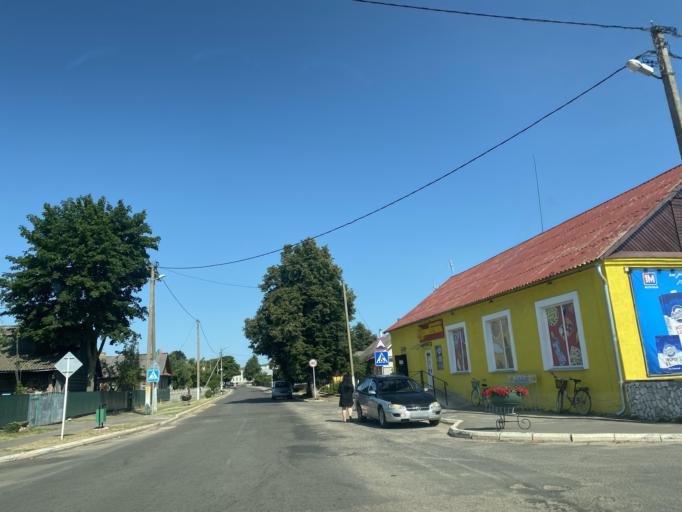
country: BY
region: Brest
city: Ivanava
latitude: 52.3151
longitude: 25.6127
